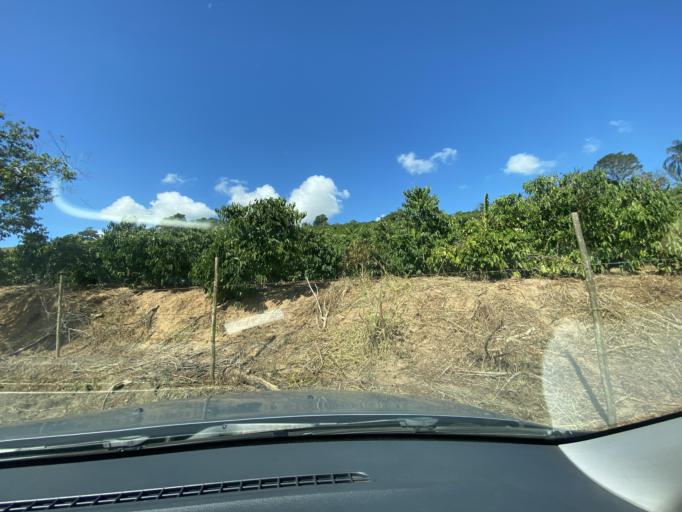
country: BR
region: Espirito Santo
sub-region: Jeronimo Monteiro
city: Jeronimo Monteiro
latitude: -20.7937
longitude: -41.4105
